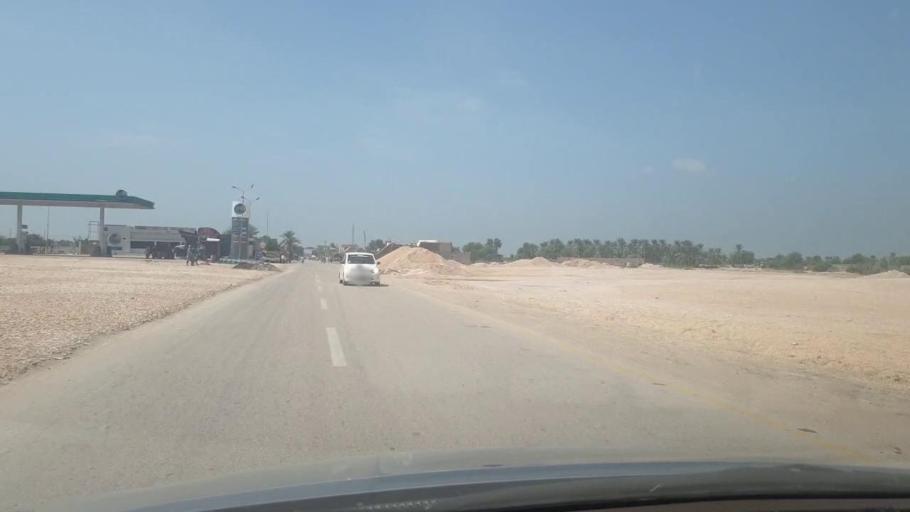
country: PK
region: Sindh
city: Bozdar
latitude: 27.2258
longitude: 68.5670
